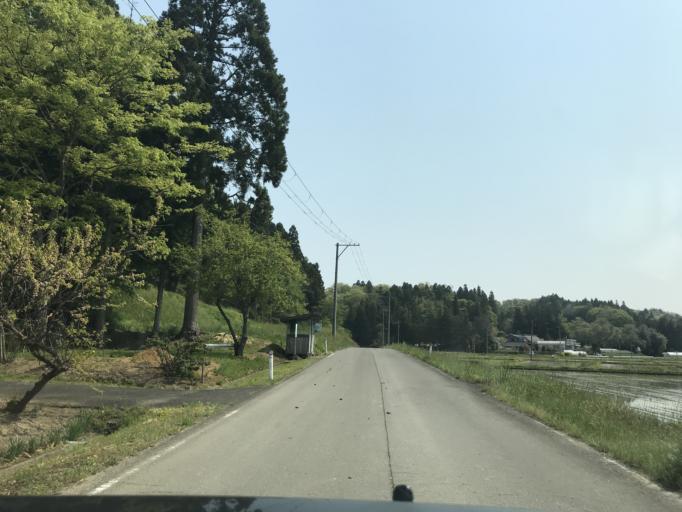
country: JP
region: Iwate
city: Ichinoseki
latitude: 38.8625
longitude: 141.0571
